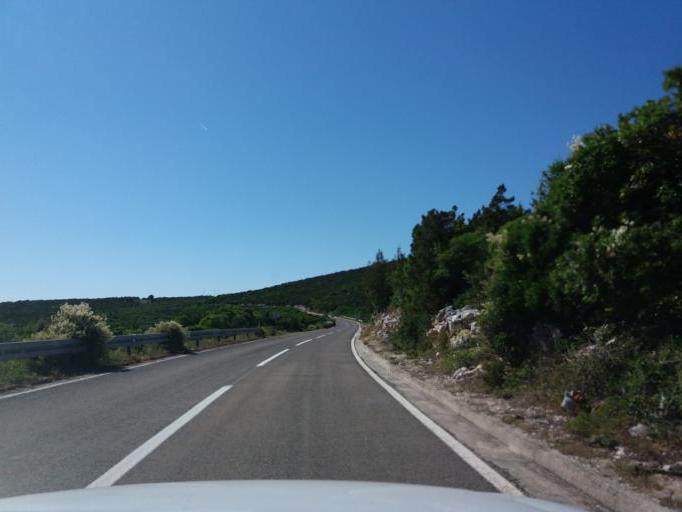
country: HR
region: Zadarska
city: Ugljan
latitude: 44.0846
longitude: 14.9698
